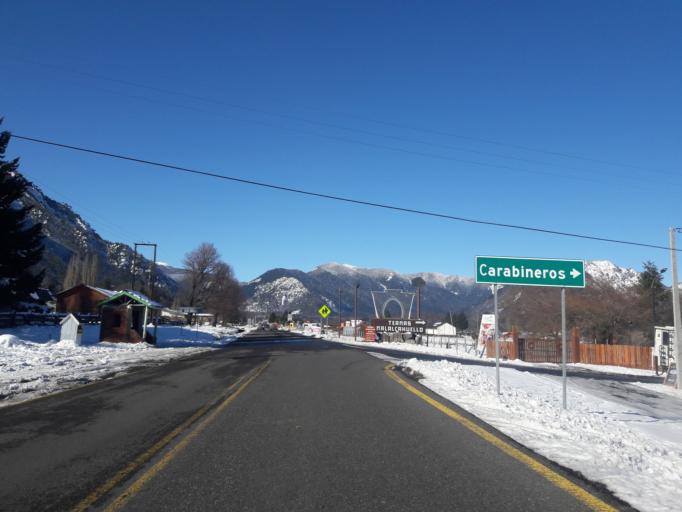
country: CL
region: Araucania
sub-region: Provincia de Cautin
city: Vilcun
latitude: -38.4710
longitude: -71.5783
